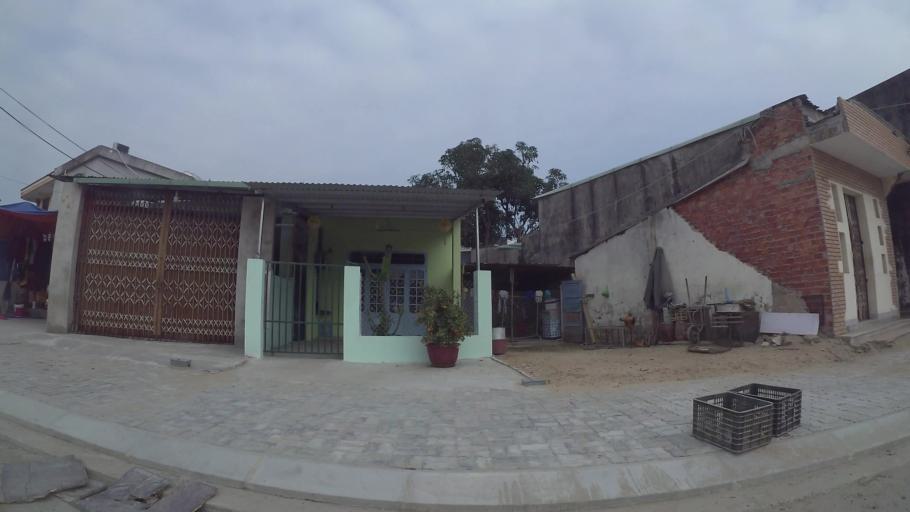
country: VN
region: Da Nang
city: Son Tra
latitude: 16.0651
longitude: 108.2398
